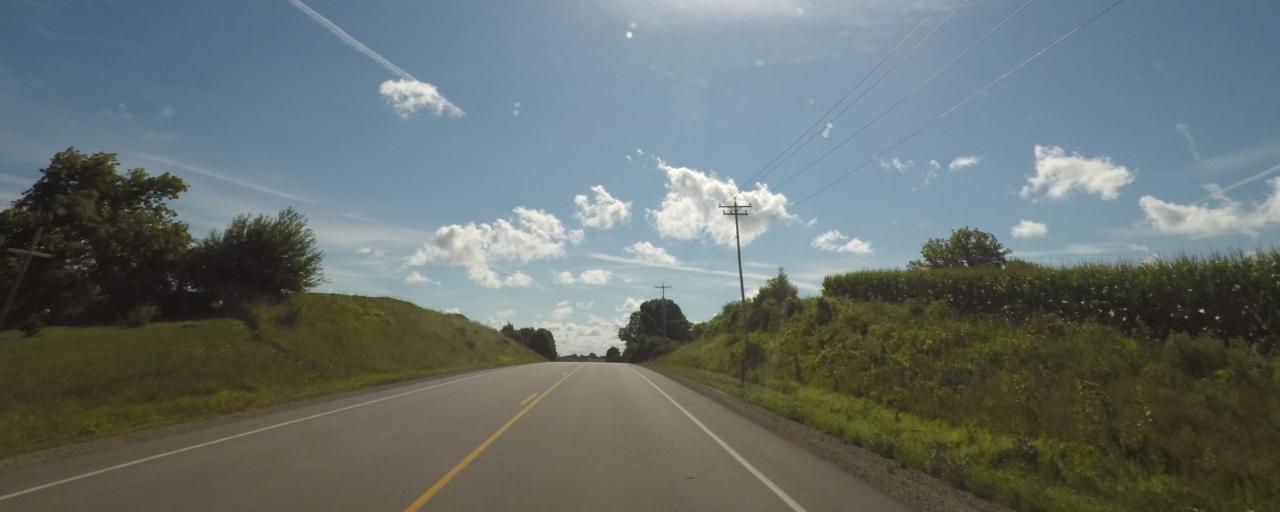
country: US
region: Wisconsin
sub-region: Jefferson County
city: Ixonia
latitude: 43.0678
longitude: -88.6195
